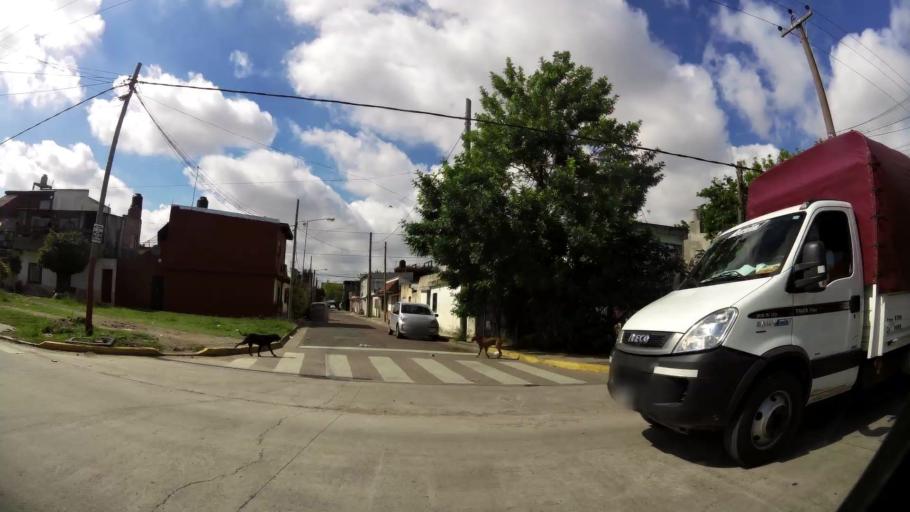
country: AR
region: Buenos Aires F.D.
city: Villa Lugano
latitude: -34.6800
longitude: -58.4322
